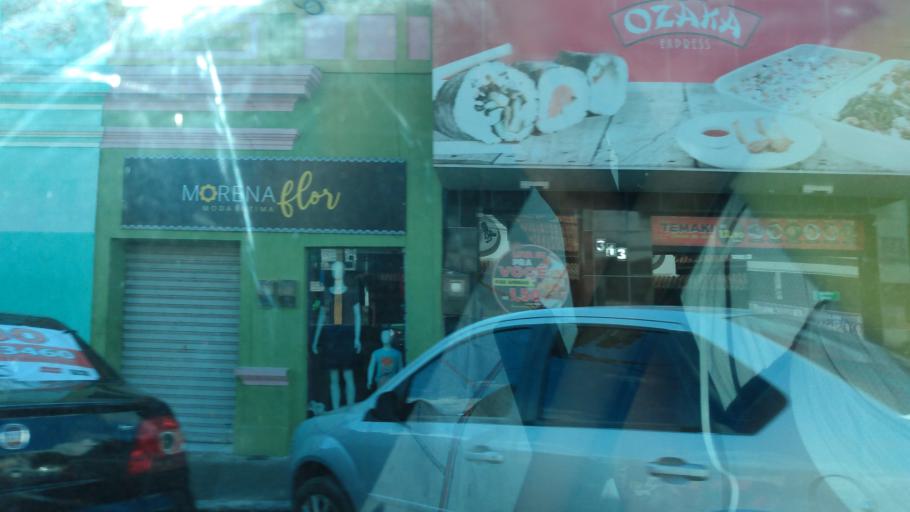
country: ET
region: Oromiya
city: Gore
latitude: 8.1999
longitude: 35.5641
